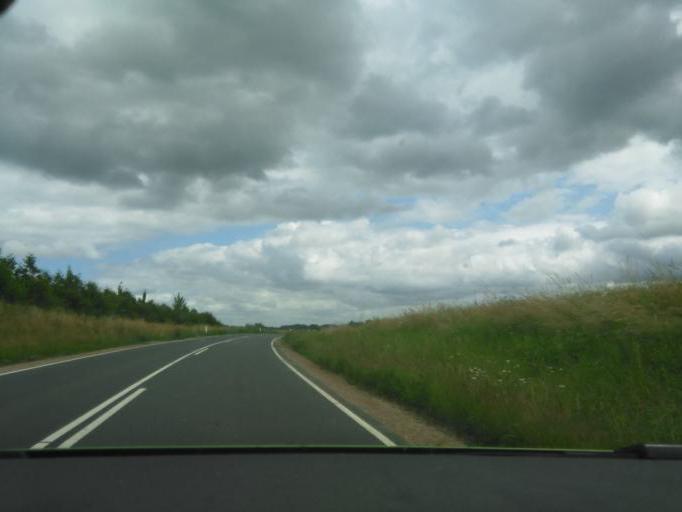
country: DK
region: Zealand
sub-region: Kalundborg Kommune
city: Hong
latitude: 55.5453
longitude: 11.2816
